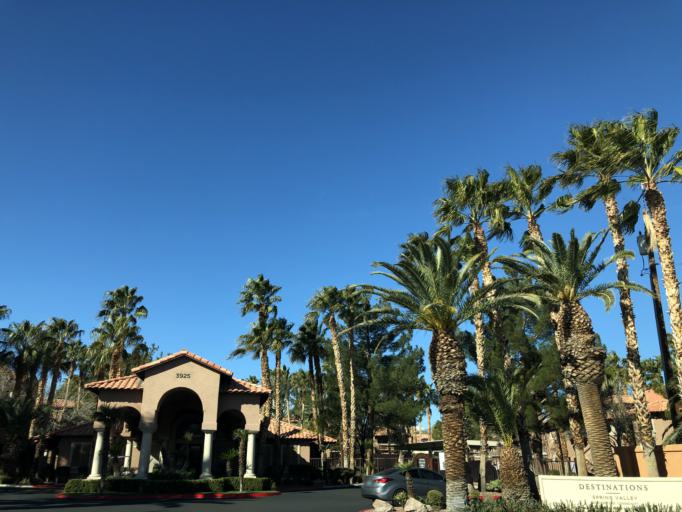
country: US
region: Nevada
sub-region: Clark County
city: Spring Valley
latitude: 36.1180
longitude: -115.2263
